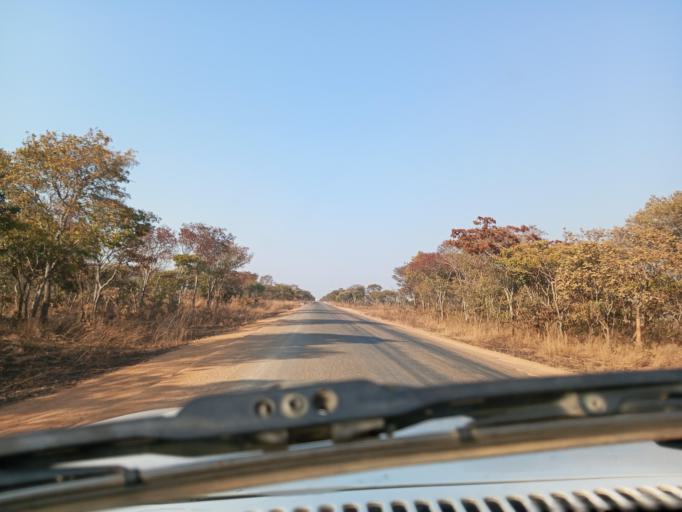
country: ZM
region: Northern
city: Mpika
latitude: -12.4027
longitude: 31.0878
